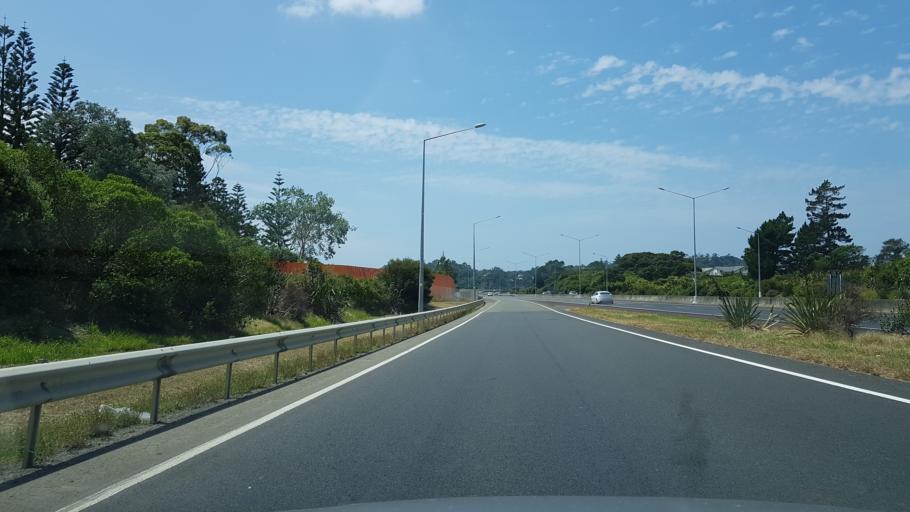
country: NZ
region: Auckland
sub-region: Auckland
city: Rosebank
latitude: -36.7898
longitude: 174.6562
